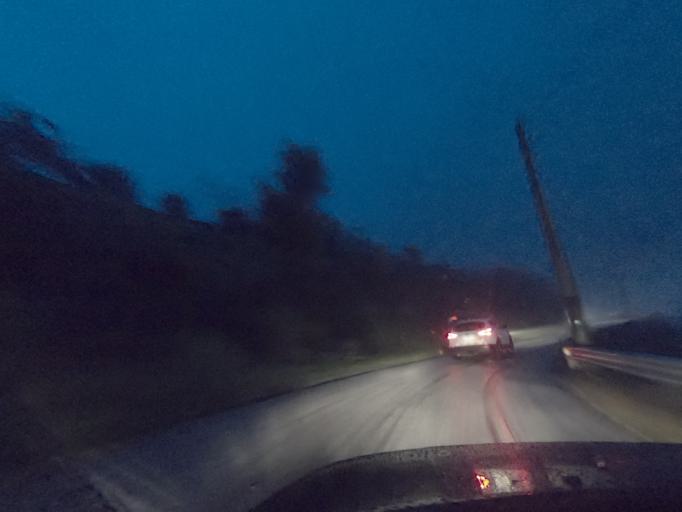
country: PT
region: Vila Real
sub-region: Sabrosa
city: Vilela
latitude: 41.2117
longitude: -7.5550
